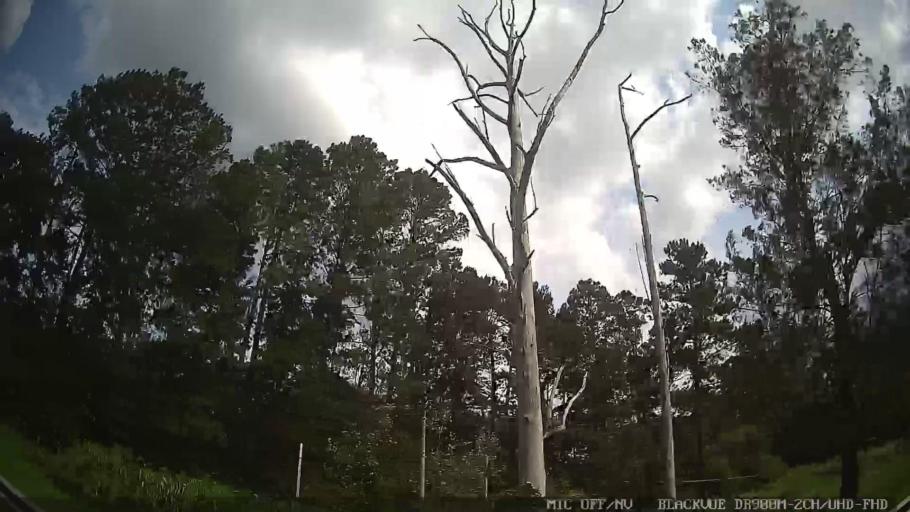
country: BR
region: Sao Paulo
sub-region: Itatiba
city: Itatiba
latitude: -23.0533
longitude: -46.8891
